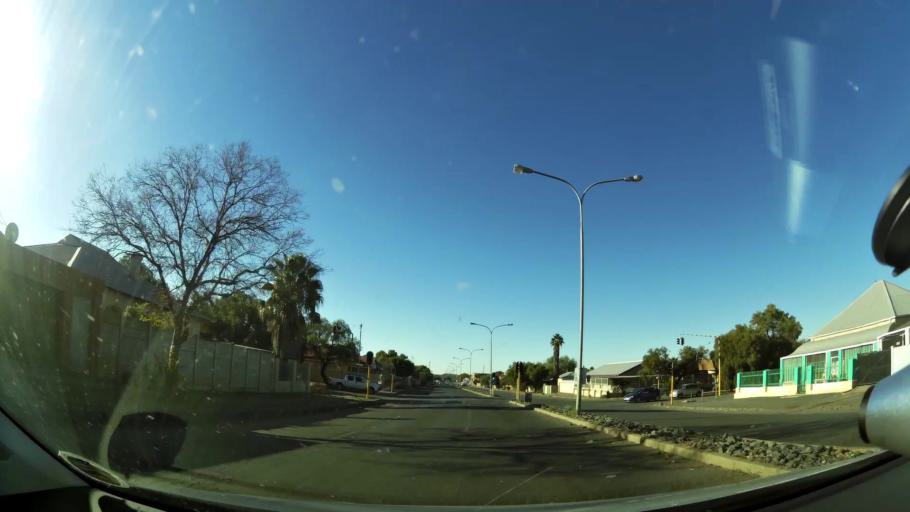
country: ZA
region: Northern Cape
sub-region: Frances Baard District Municipality
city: Kimberley
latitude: -28.7548
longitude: 24.7820
